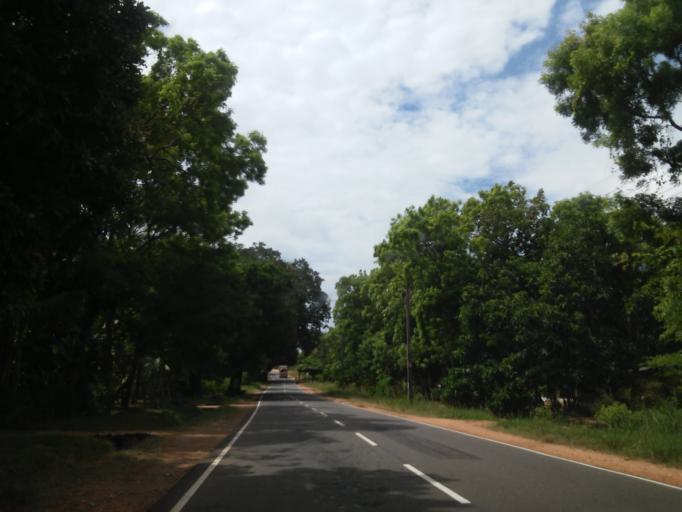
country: LK
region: Central
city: Sigiriya
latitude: 8.0691
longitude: 80.6966
